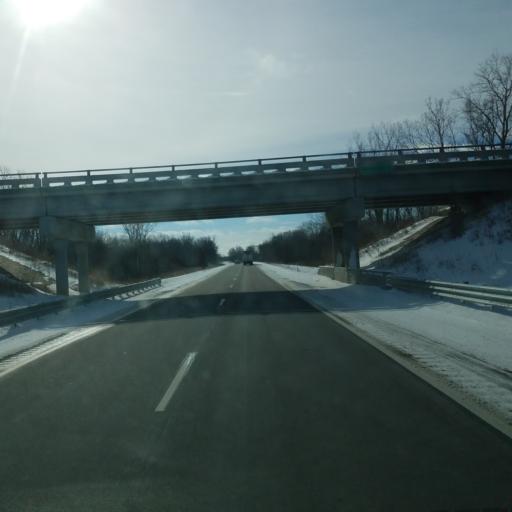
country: US
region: Michigan
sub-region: Gratiot County
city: Ithaca
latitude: 43.3357
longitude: -84.6024
